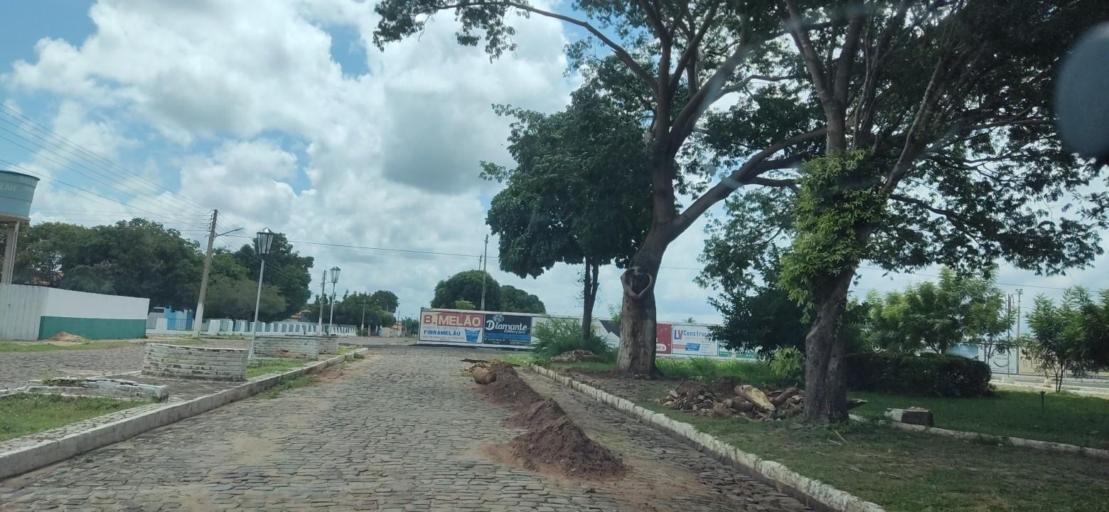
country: BR
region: Piaui
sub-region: Valenca Do Piaui
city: Valenca do Piaui
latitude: -6.4018
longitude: -41.7354
